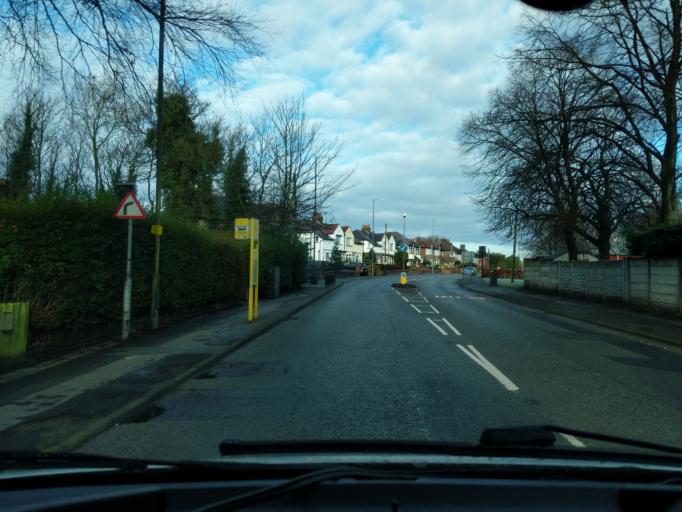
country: GB
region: England
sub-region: St. Helens
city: Eccleston
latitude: 53.4655
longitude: -2.7635
